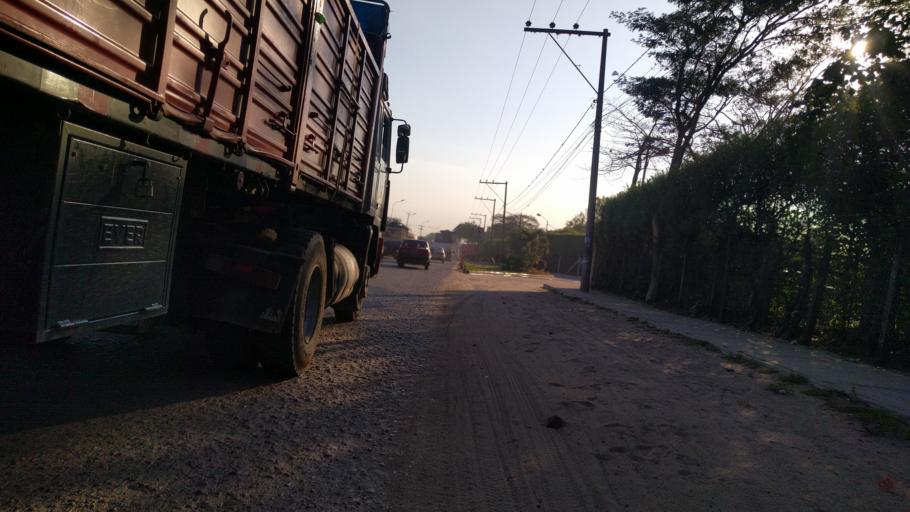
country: BO
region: Santa Cruz
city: Santa Cruz de la Sierra
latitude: -17.8133
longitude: -63.1631
